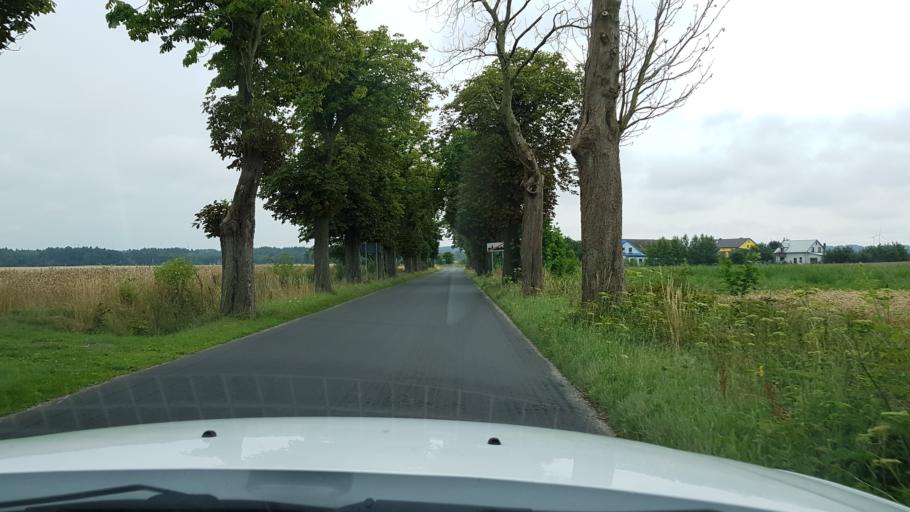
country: PL
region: West Pomeranian Voivodeship
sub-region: Powiat slawienski
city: Slawno
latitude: 54.5062
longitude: 16.5738
